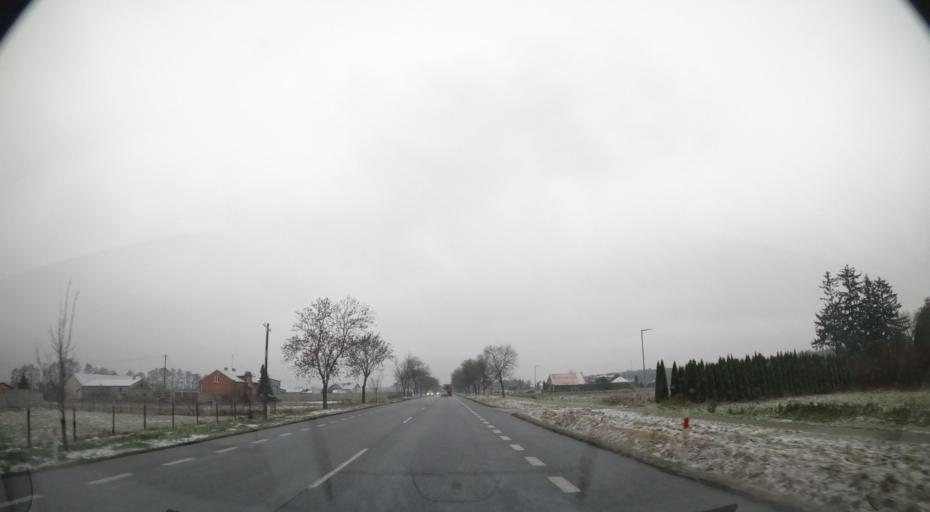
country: PL
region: Masovian Voivodeship
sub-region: Powiat sochaczewski
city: Sochaczew
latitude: 52.2237
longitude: 20.3017
